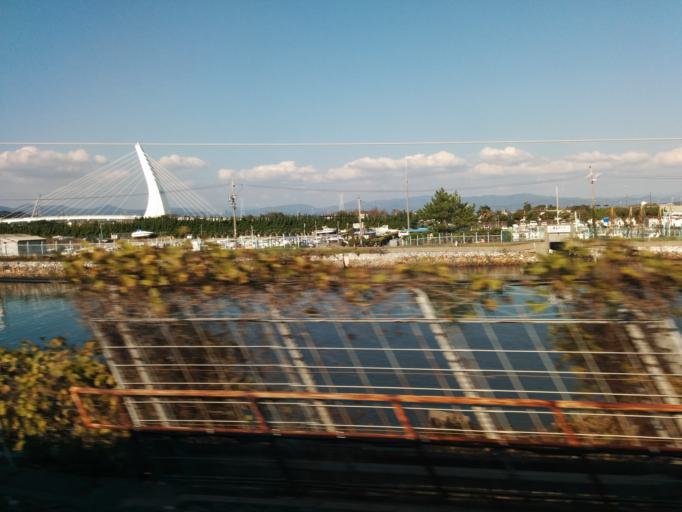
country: JP
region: Shizuoka
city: Kosai-shi
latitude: 34.6949
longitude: 137.5680
